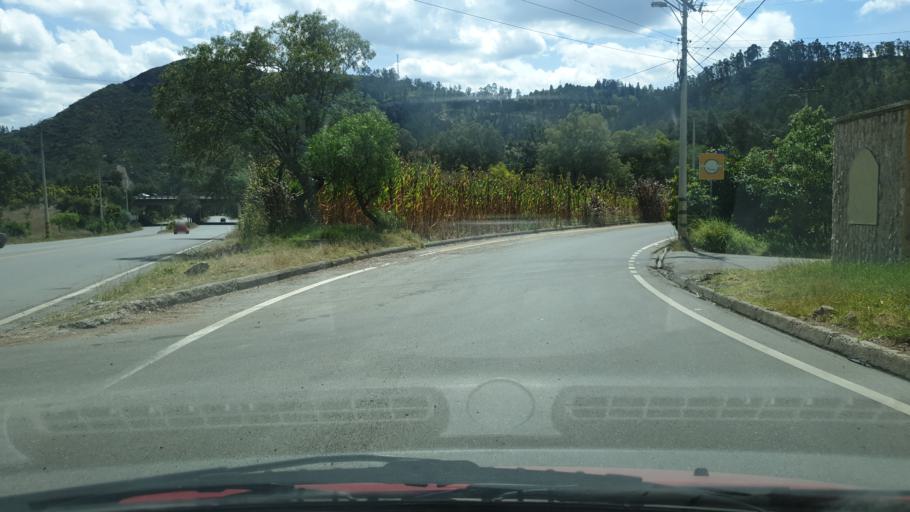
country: EC
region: Azuay
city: Llacao
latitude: -2.8461
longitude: -78.8814
